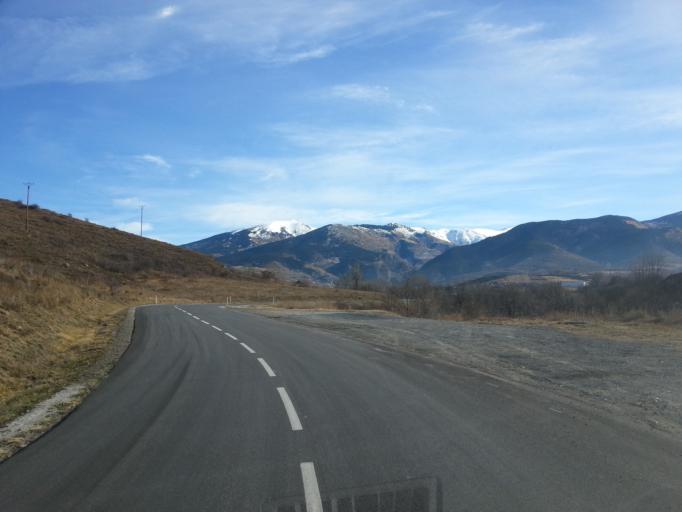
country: ES
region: Catalonia
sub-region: Provincia de Girona
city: Llivia
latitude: 42.4610
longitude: 2.0153
